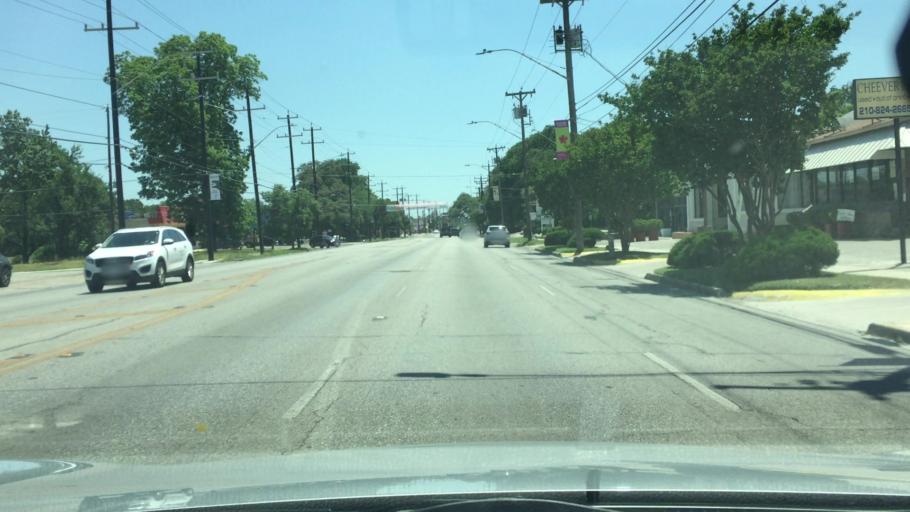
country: US
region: Texas
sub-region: Bexar County
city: Terrell Hills
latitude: 29.4598
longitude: -98.4678
